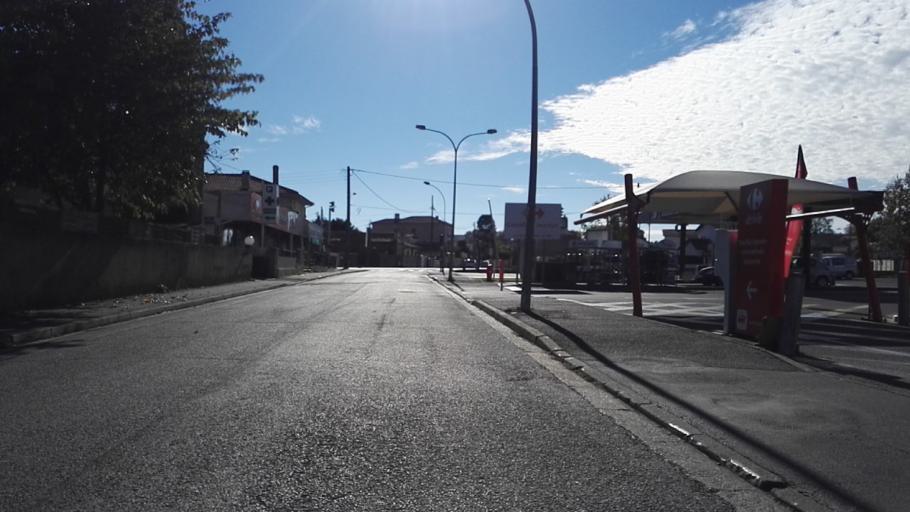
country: FR
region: Aquitaine
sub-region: Departement de la Gironde
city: Eysines
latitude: 44.8609
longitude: -0.6338
